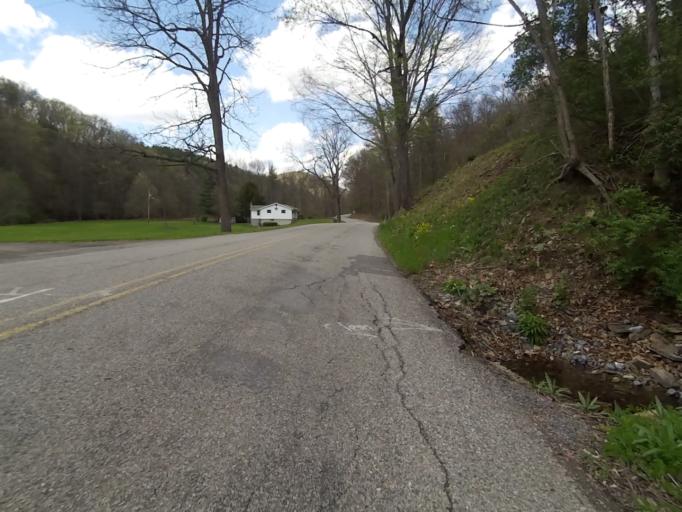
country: US
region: Pennsylvania
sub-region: Centre County
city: Milesburg
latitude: 40.9314
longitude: -77.8750
